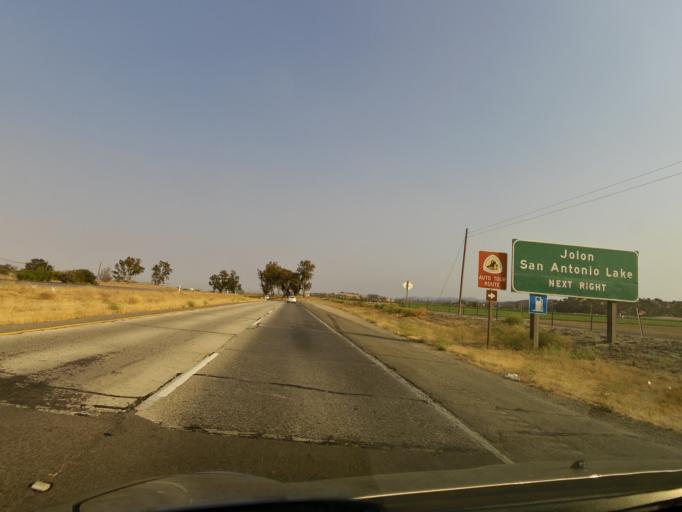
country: US
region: California
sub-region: Monterey County
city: King City
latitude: 36.2006
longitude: -121.1545
